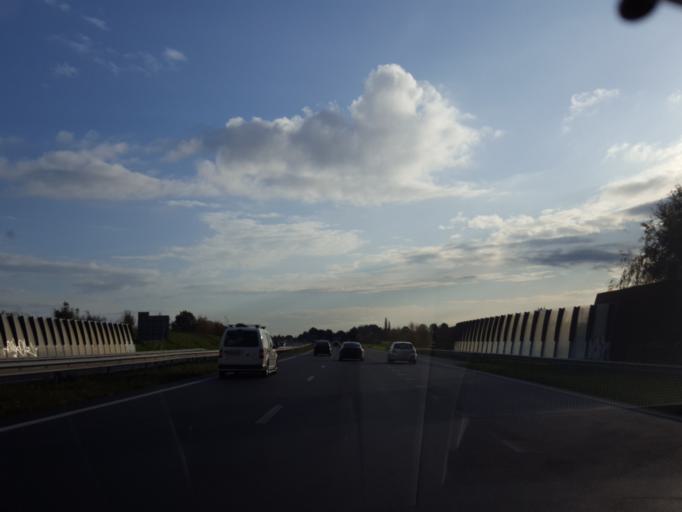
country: NL
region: North Brabant
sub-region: Gemeente Uden
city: Uden
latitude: 51.6663
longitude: 5.5997
